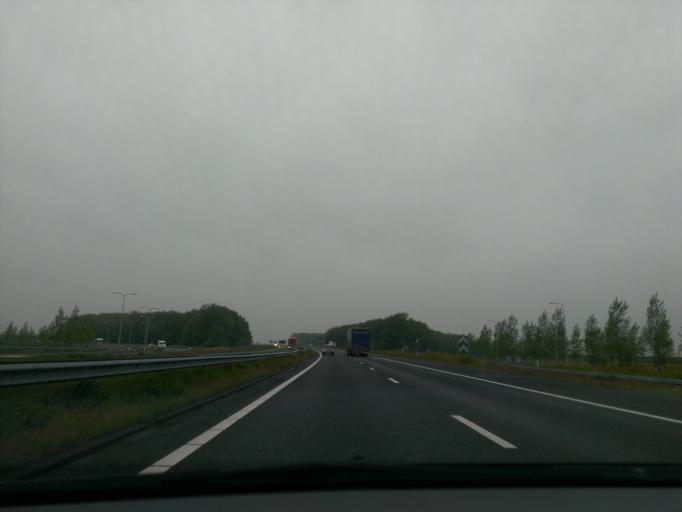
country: NL
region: Gelderland
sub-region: Gemeente Zaltbommel
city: Zaltbommel
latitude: 51.8582
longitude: 5.2372
